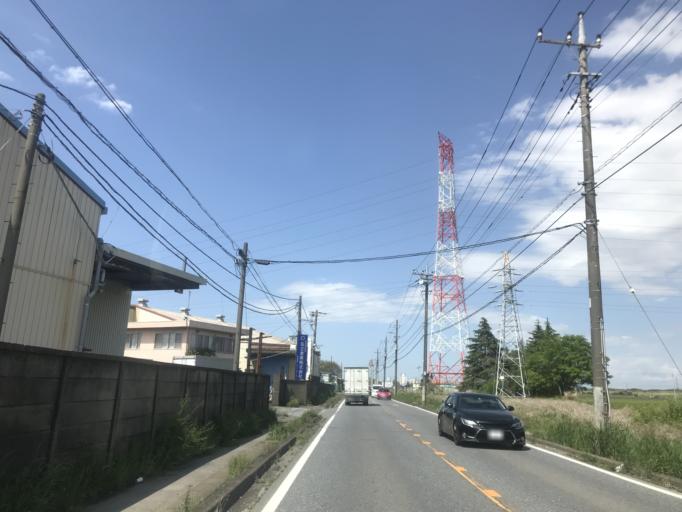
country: JP
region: Chiba
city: Noda
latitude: 35.9724
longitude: 139.8847
